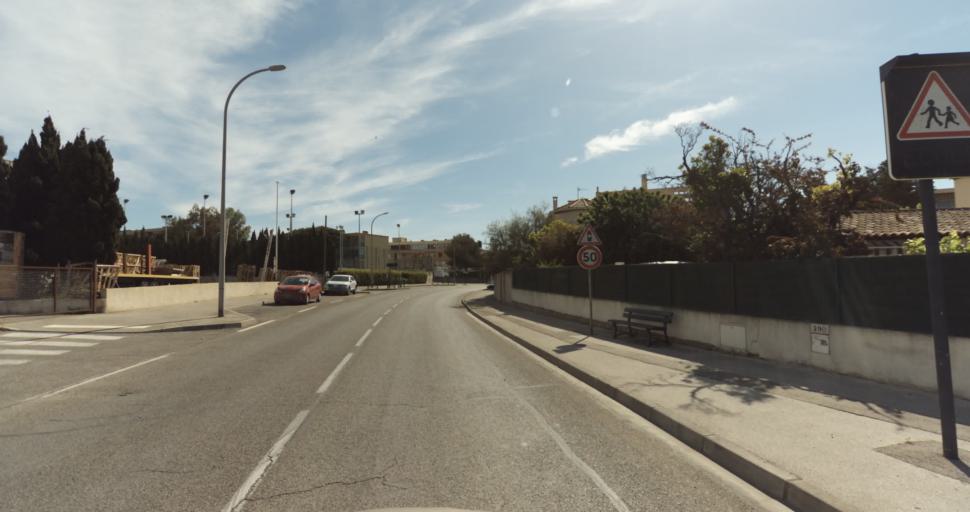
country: FR
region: Provence-Alpes-Cote d'Azur
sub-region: Departement du Var
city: Sanary-sur-Mer
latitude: 43.1075
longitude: 5.8185
